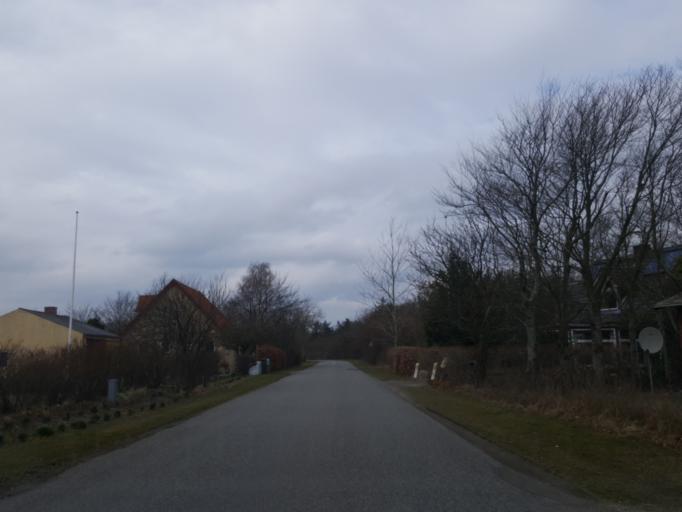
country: DK
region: Central Jutland
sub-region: Holstebro Kommune
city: Ulfborg
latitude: 56.3631
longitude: 8.2526
